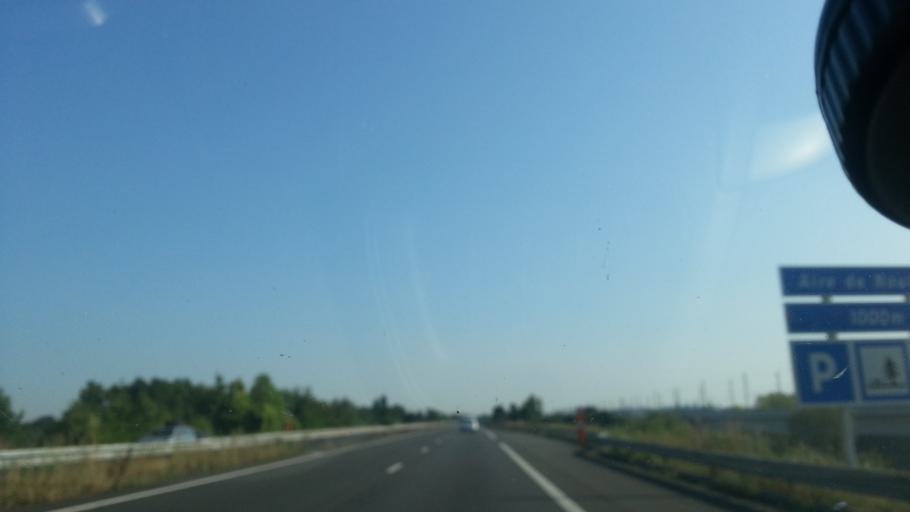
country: FR
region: Centre
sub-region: Departement d'Indre-et-Loire
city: La Celle-Saint-Avant
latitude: 47.0146
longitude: 0.5607
